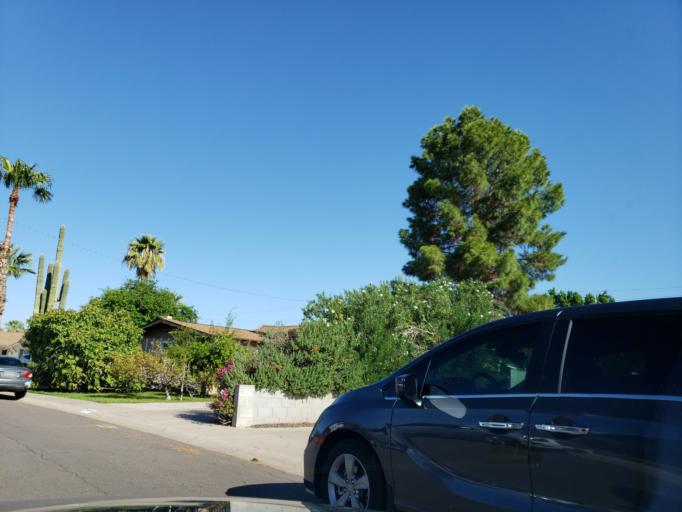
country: US
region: Arizona
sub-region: Maricopa County
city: Scottsdale
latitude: 33.5185
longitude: -111.8981
